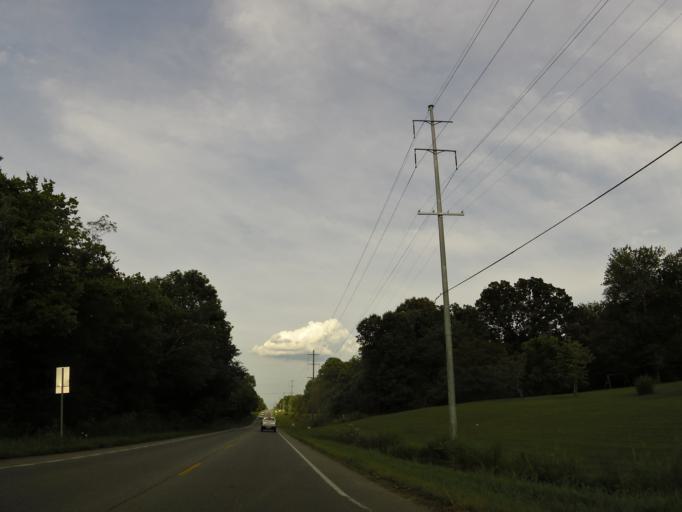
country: US
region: Tennessee
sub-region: Humphreys County
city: McEwen
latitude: 36.0912
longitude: -87.5166
